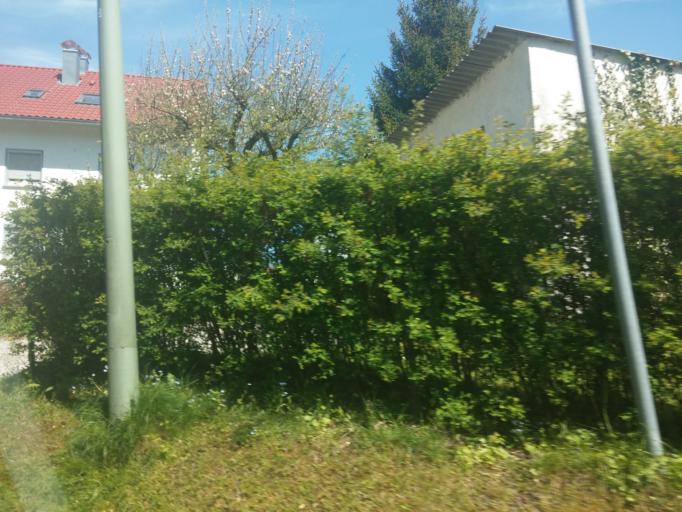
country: DE
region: Bavaria
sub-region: Swabia
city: Lautrach
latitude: 47.8997
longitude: 10.1231
